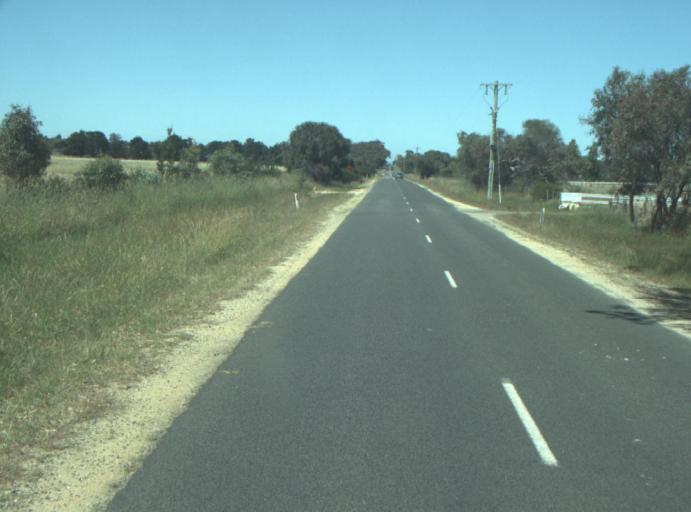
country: AU
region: Victoria
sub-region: Greater Geelong
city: Breakwater
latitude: -38.2446
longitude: 144.3520
